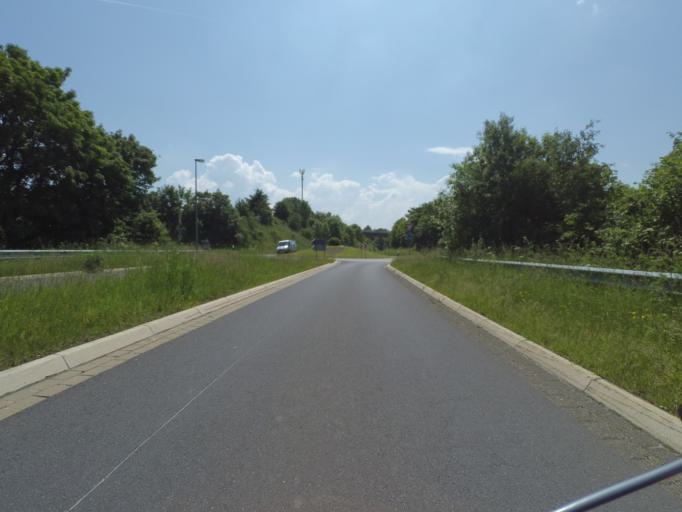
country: DE
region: Rheinland-Pfalz
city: Kaisersesch
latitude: 50.2345
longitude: 7.1474
